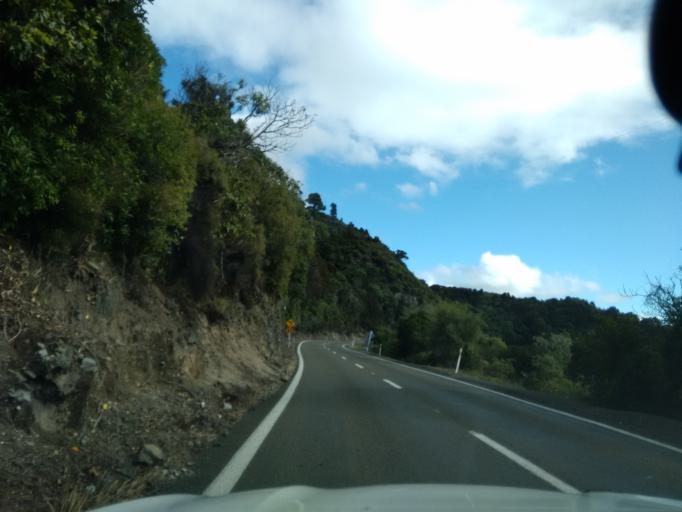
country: NZ
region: Waikato
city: Turangi
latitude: -38.8815
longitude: 175.9707
